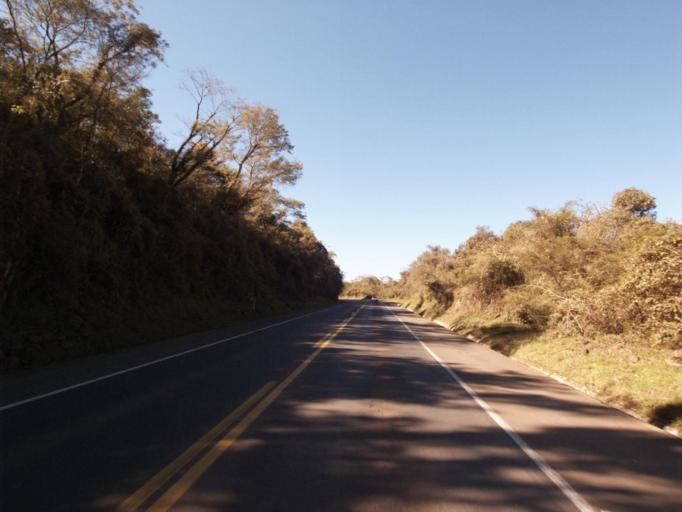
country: BR
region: Santa Catarina
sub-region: Chapeco
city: Chapeco
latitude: -26.9739
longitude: -52.5853
